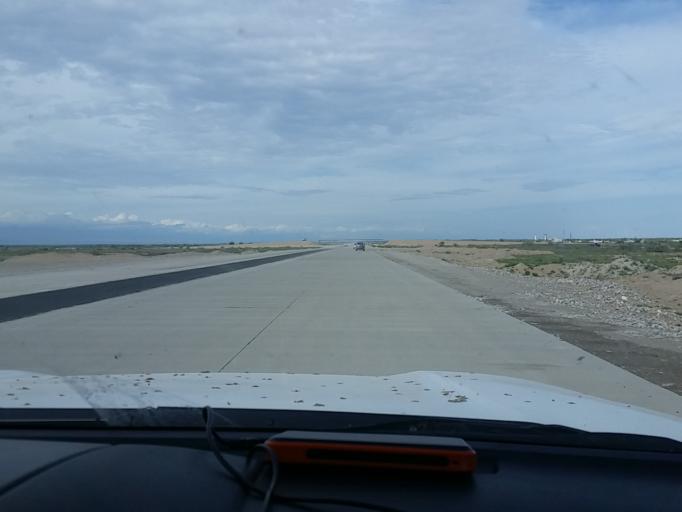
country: KZ
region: Almaty Oblysy
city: Zharkent
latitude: 44.0412
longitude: 79.9701
